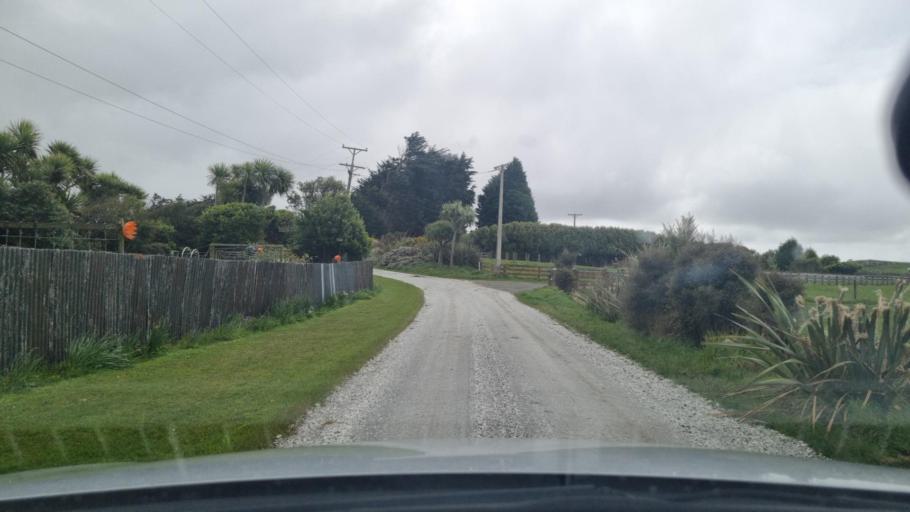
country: NZ
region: Southland
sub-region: Invercargill City
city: Bluff
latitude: -46.5392
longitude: 168.2904
